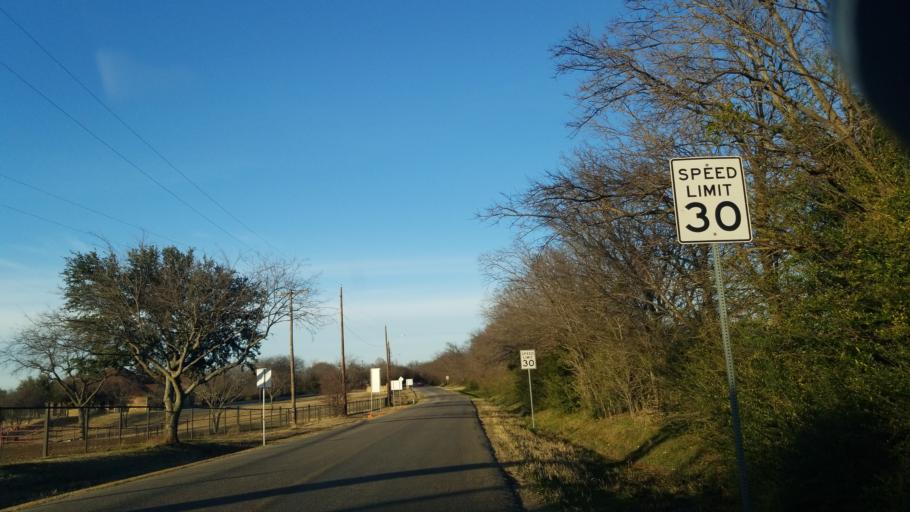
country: US
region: Texas
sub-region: Denton County
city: Denton
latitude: 33.1839
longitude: -97.1631
